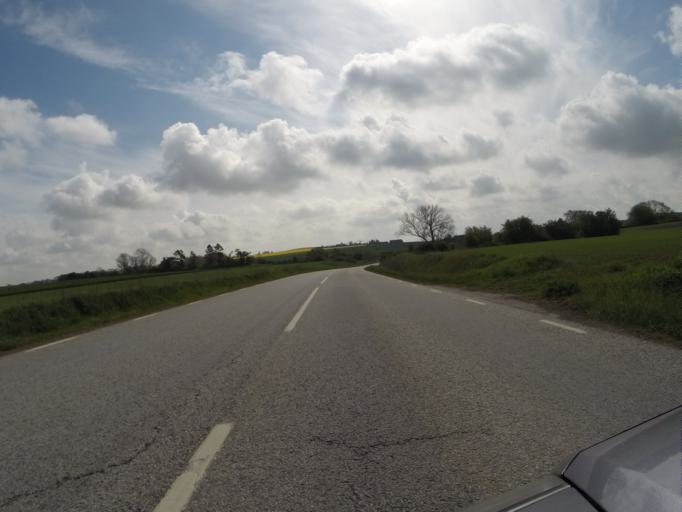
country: SE
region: Skane
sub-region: Kavlinge Kommun
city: Loddekopinge
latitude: 55.8317
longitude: 13.0272
